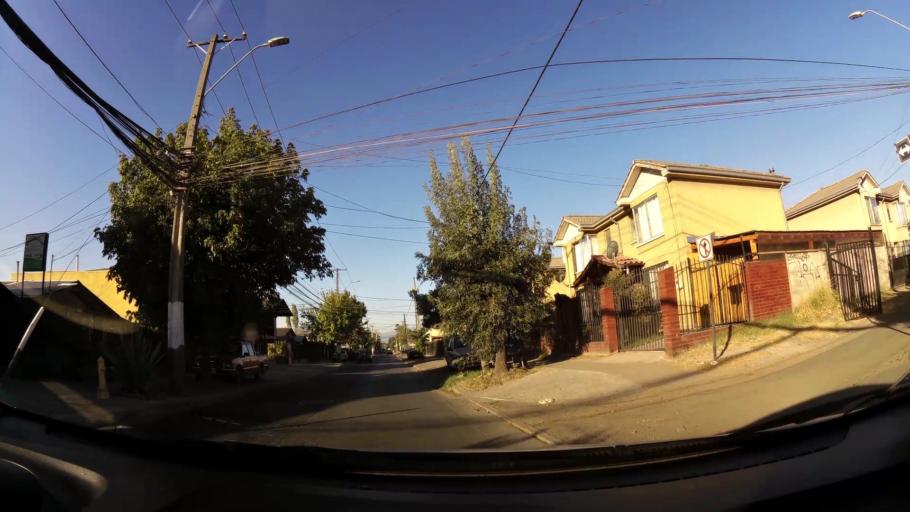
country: CL
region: O'Higgins
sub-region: Provincia de Cachapoal
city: Rancagua
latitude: -34.1762
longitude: -70.7610
